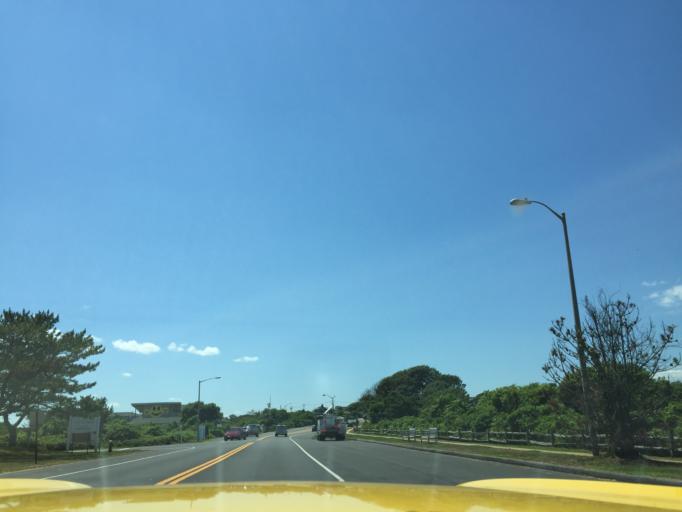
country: US
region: New York
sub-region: Suffolk County
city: Montauk
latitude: 41.0315
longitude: -71.9502
